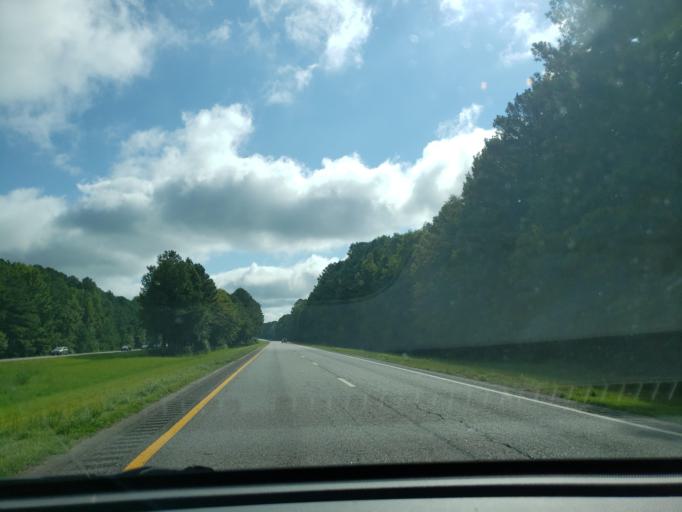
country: US
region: North Carolina
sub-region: Nash County
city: Nashville
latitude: 35.9465
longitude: -78.0341
